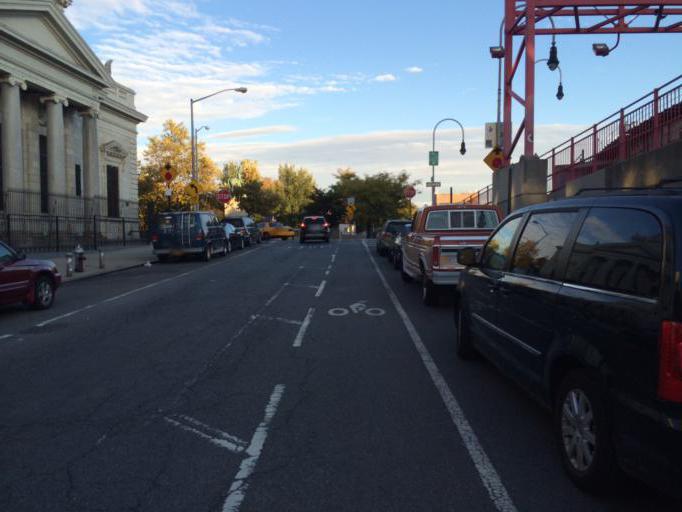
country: US
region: New York
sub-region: Queens County
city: Long Island City
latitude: 40.7107
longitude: -73.9615
